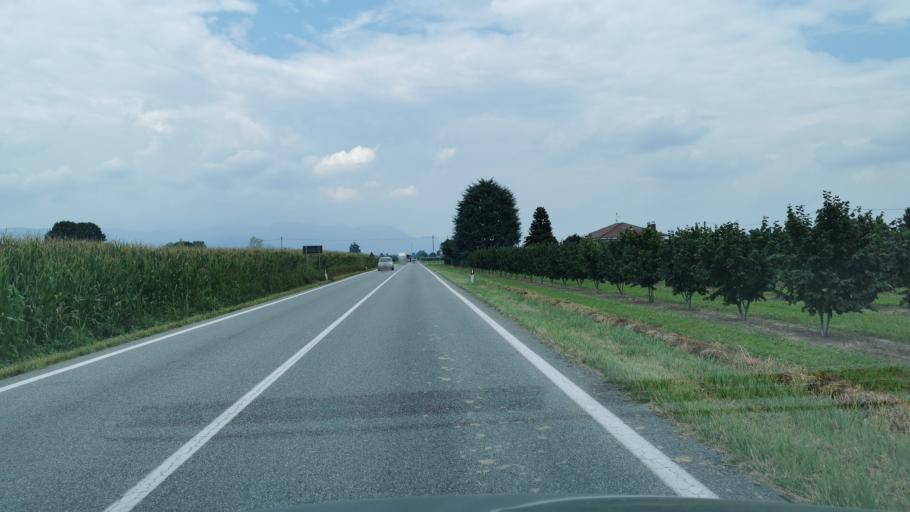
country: IT
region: Piedmont
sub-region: Provincia di Torino
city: Cavour
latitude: 44.8091
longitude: 7.3724
